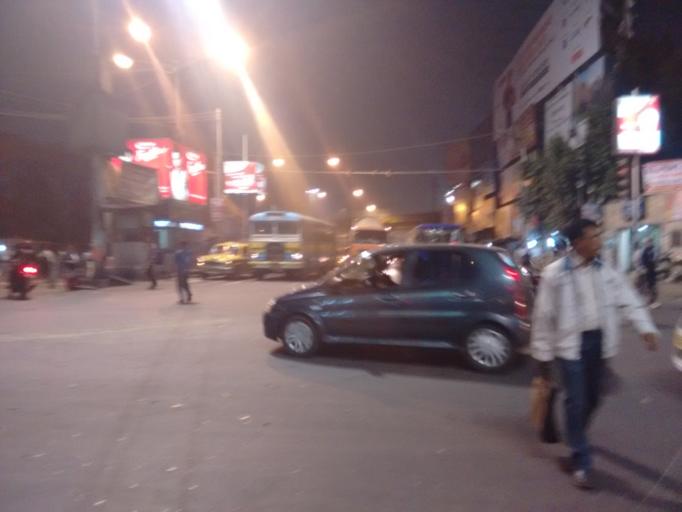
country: IN
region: West Bengal
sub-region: North 24 Parganas
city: Dam Dam
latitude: 22.6420
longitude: 88.4310
